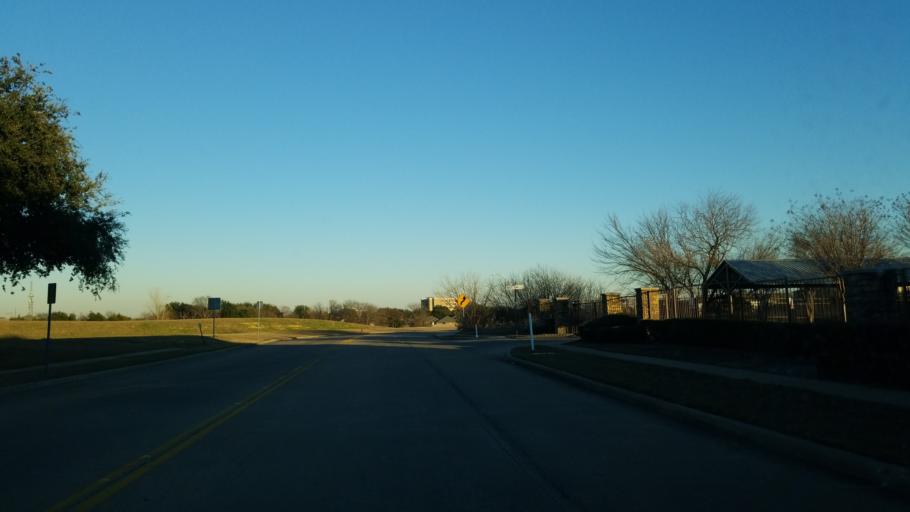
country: US
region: Texas
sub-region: Tarrant County
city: Arlington
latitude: 32.7332
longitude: -97.0572
